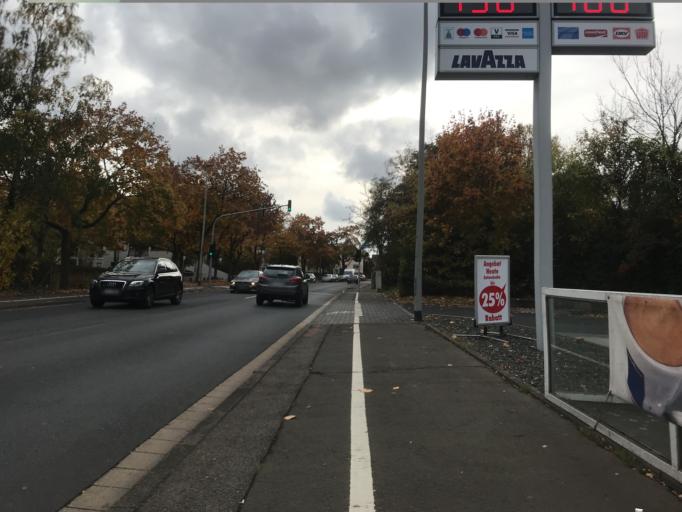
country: DE
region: Rheinland-Pfalz
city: Budenheim
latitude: 50.0200
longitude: 8.2207
